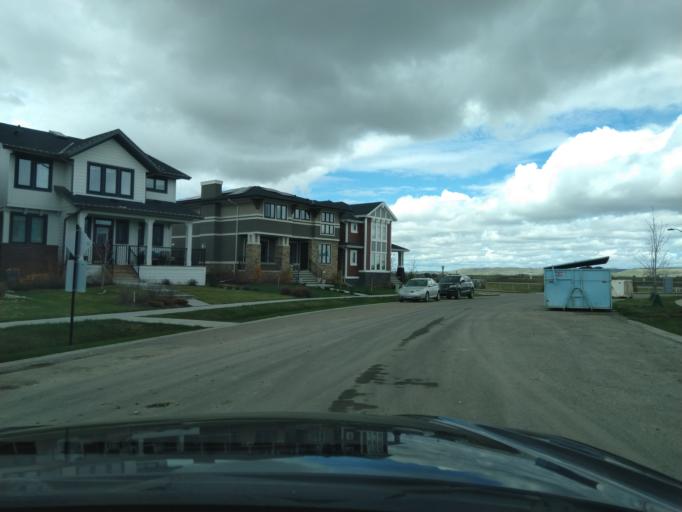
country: CA
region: Alberta
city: Cochrane
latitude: 51.1123
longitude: -114.3965
